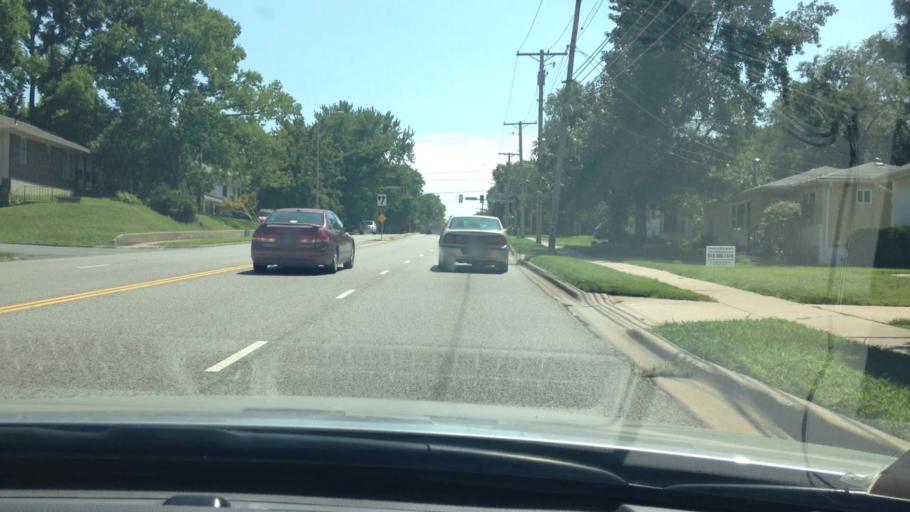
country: US
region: Kansas
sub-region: Johnson County
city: Overland Park
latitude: 38.9871
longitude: -94.6864
